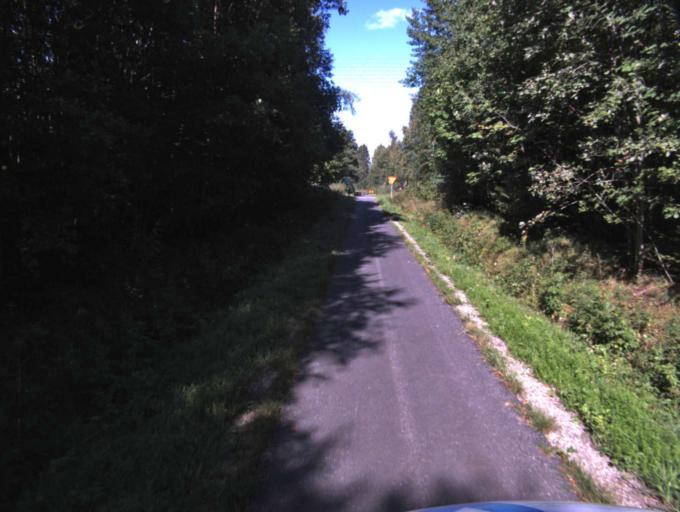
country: SE
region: Vaestra Goetaland
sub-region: Ulricehamns Kommun
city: Ulricehamn
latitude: 57.8116
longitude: 13.3548
